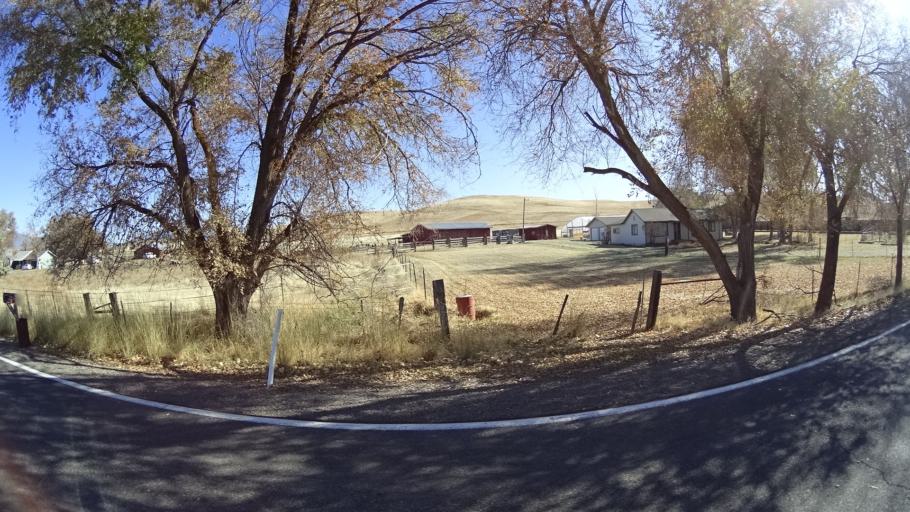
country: US
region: California
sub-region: Siskiyou County
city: Montague
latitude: 41.7421
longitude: -122.5104
